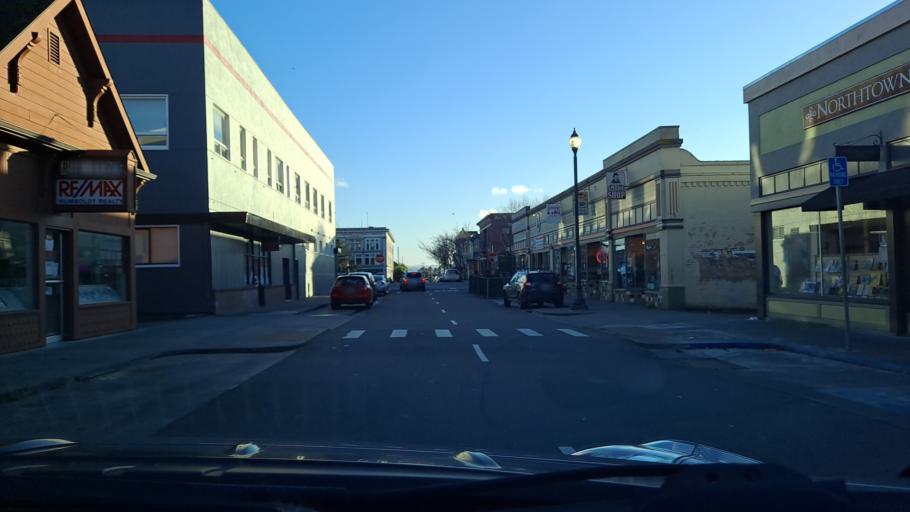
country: US
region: California
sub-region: Humboldt County
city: Arcata
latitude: 40.8696
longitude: -124.0866
